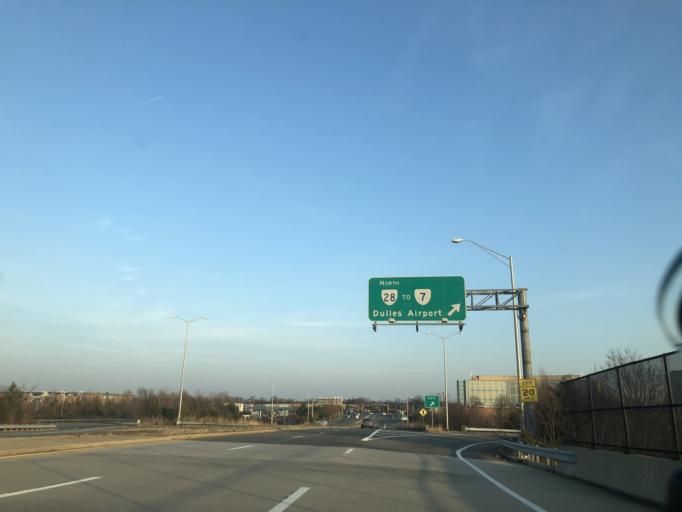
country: US
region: Virginia
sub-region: Fairfax County
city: Chantilly
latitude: 38.9151
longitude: -77.4298
